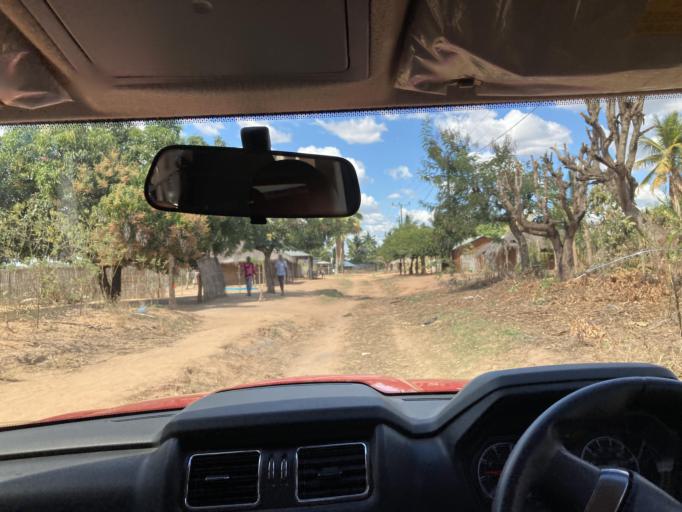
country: MZ
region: Cabo Delgado
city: Montepuez
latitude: -13.1487
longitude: 38.9891
